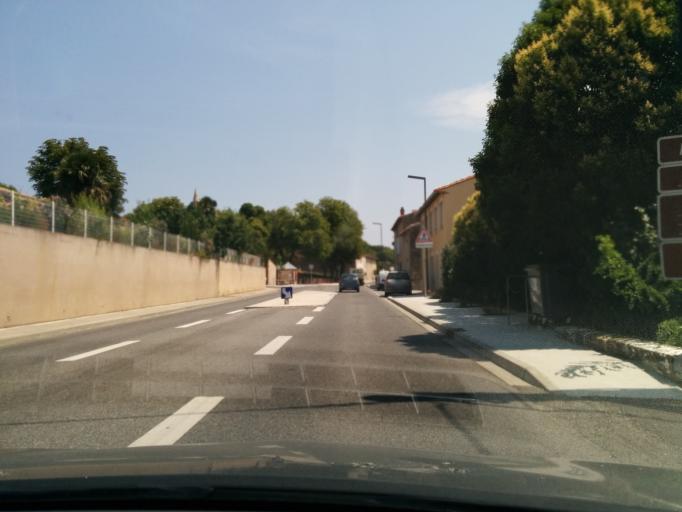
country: FR
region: Midi-Pyrenees
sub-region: Departement de la Haute-Garonne
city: Avignonet-Lauragais
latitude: 43.3669
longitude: 1.7827
